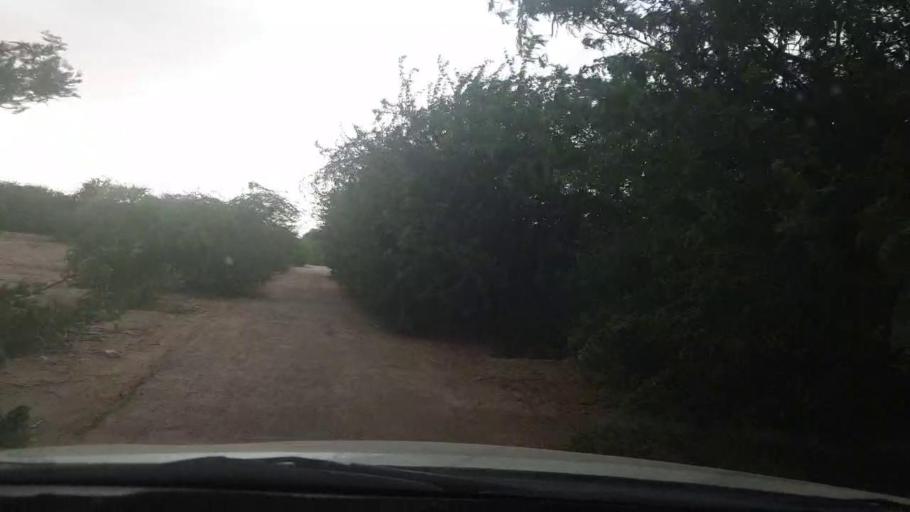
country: PK
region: Sindh
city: Khairpur
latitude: 27.4443
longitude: 68.9905
